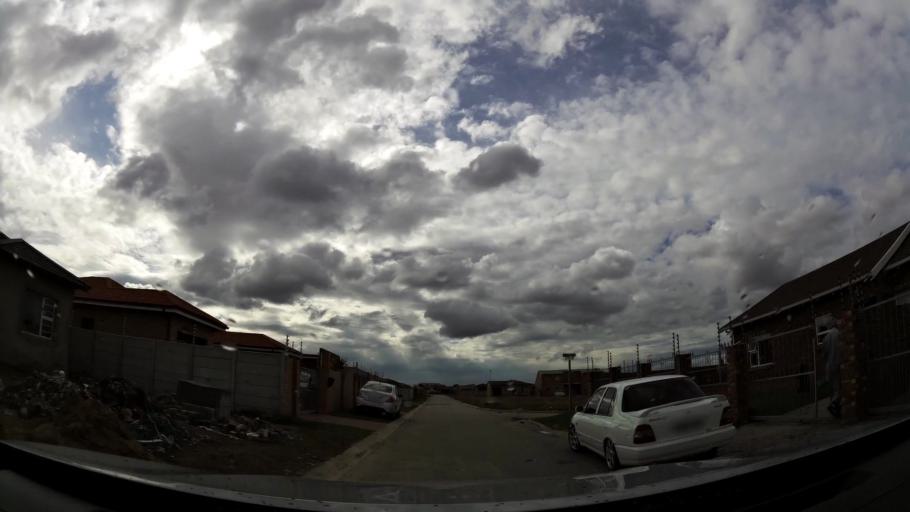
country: ZA
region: Eastern Cape
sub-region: Nelson Mandela Bay Metropolitan Municipality
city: Port Elizabeth
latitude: -33.9300
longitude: 25.5070
